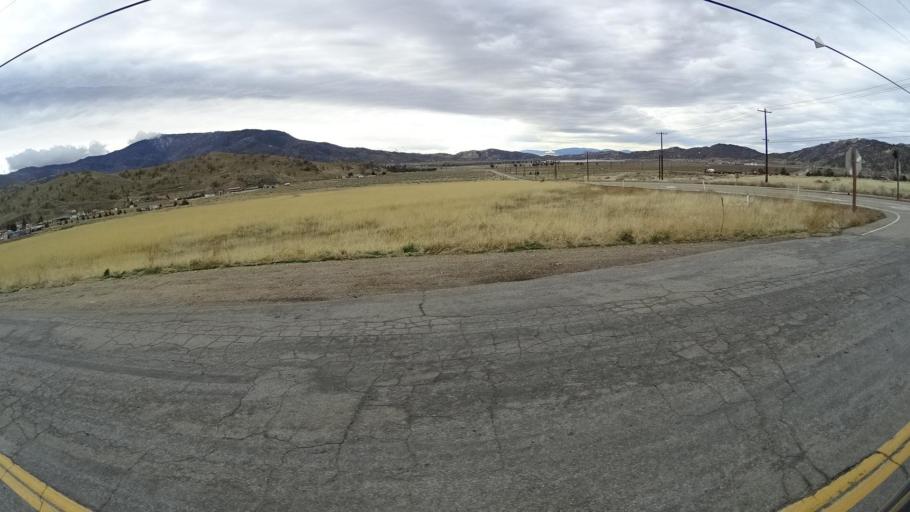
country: US
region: California
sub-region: Kern County
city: Bear Valley Springs
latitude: 35.1324
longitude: -118.5680
